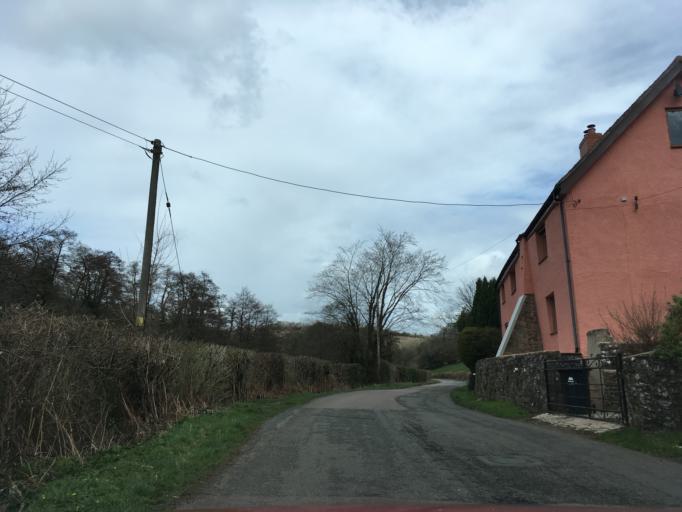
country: GB
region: England
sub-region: Gloucestershire
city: Coleford
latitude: 51.7797
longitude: -2.6325
